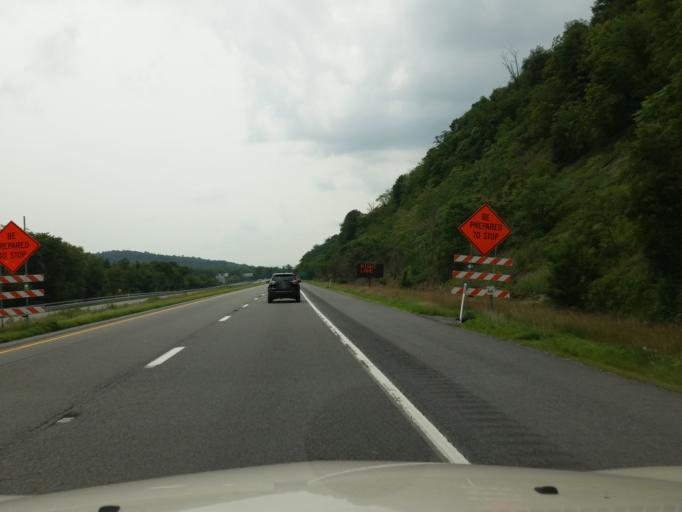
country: US
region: Pennsylvania
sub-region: Perry County
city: Newport
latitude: 40.5655
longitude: -77.1795
